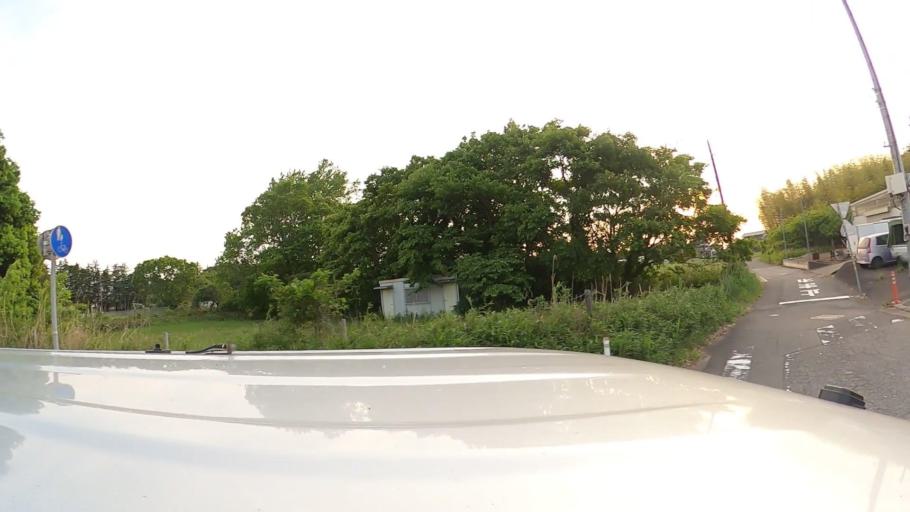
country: JP
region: Ibaraki
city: Ushiku
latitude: 36.0127
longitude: 140.1324
